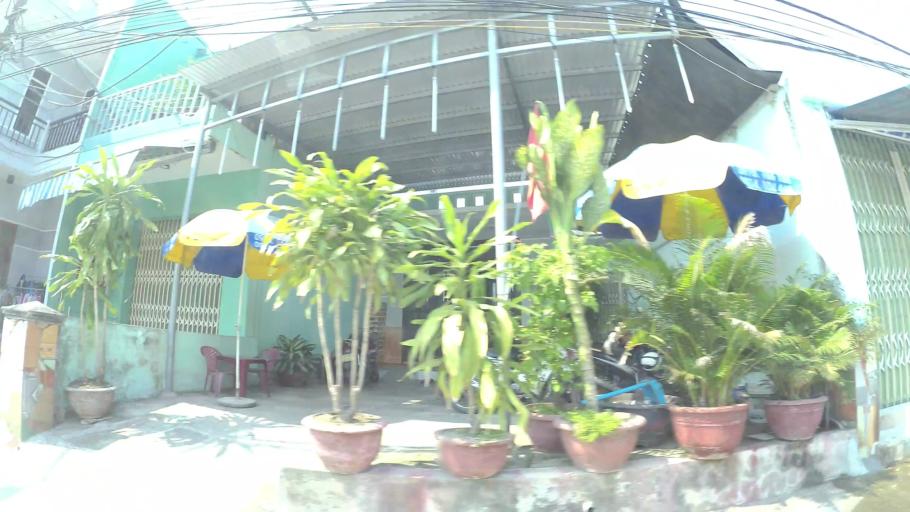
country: VN
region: Da Nang
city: Cam Le
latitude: 16.0103
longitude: 108.2014
